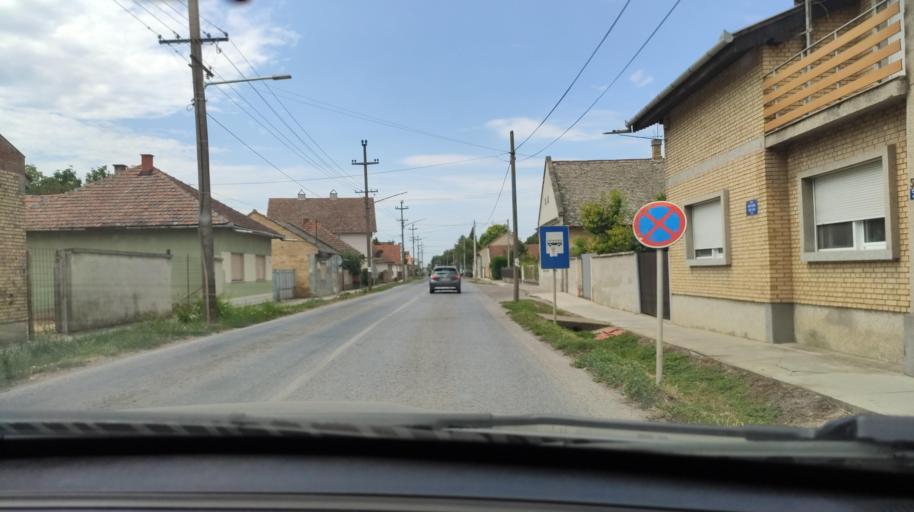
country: RS
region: Autonomna Pokrajina Vojvodina
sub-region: Juznobacki Okrug
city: Temerin
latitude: 45.4152
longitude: 19.8954
